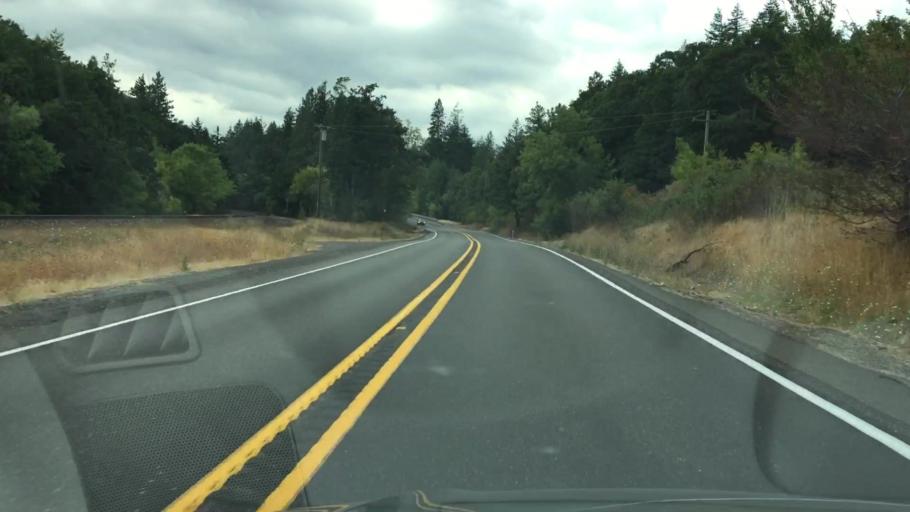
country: US
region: Washington
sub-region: Skamania County
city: Carson
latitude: 45.6998
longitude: -121.7238
